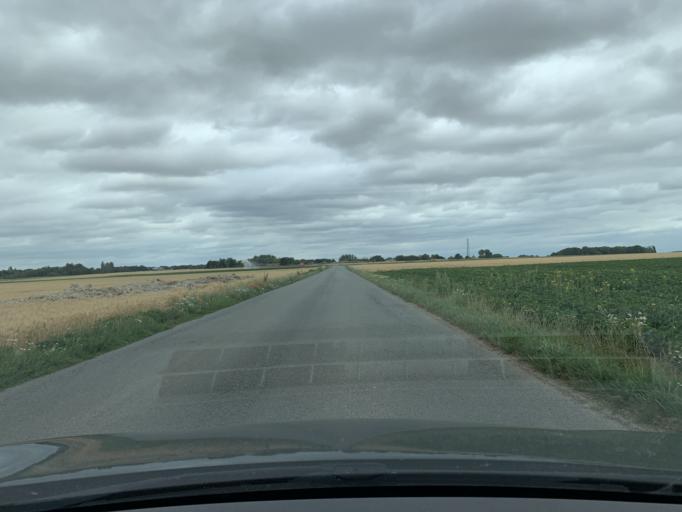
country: FR
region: Nord-Pas-de-Calais
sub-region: Departement du Nord
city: Raillencourt-Sainte-Olle
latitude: 50.2014
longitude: 3.1403
